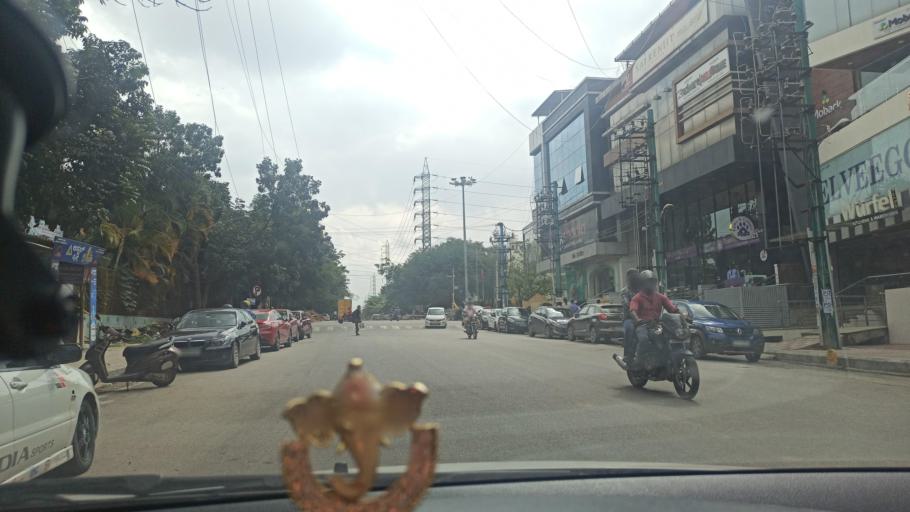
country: IN
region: Karnataka
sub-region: Bangalore Urban
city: Bangalore
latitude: 12.9129
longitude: 77.6447
